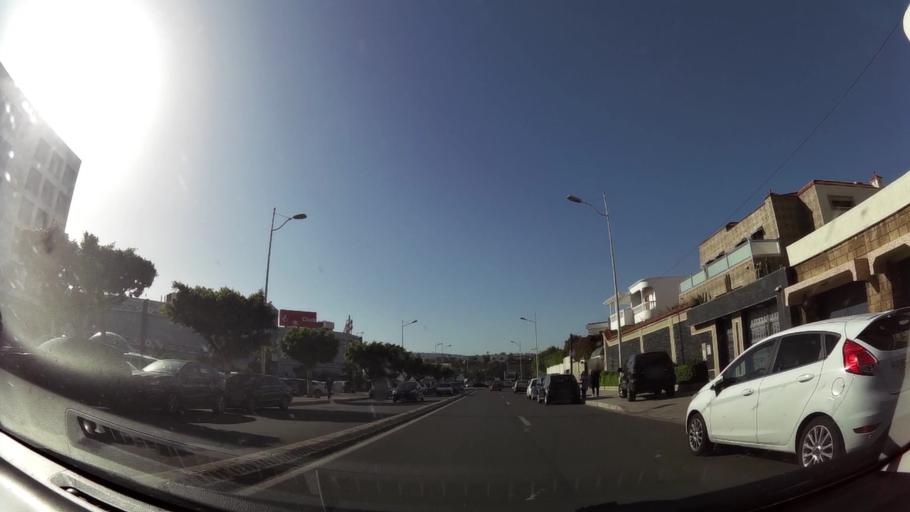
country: MA
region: Souss-Massa-Draa
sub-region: Agadir-Ida-ou-Tnan
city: Agadir
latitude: 30.4260
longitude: -9.5914
